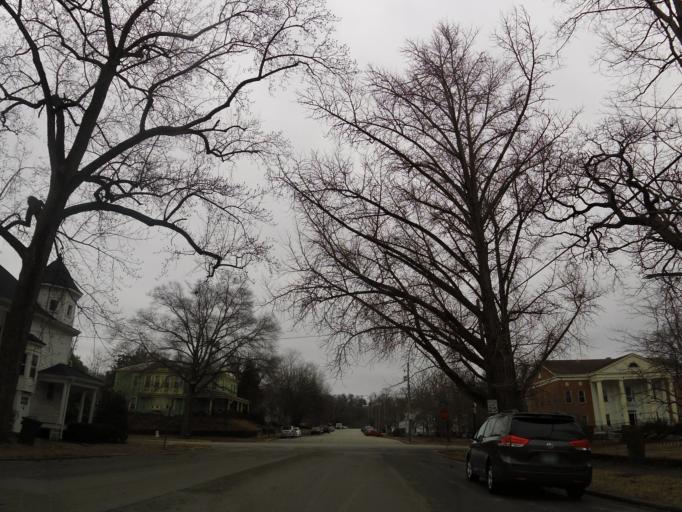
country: US
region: Kentucky
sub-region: Franklin County
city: Frankfort
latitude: 38.1922
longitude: -84.8755
